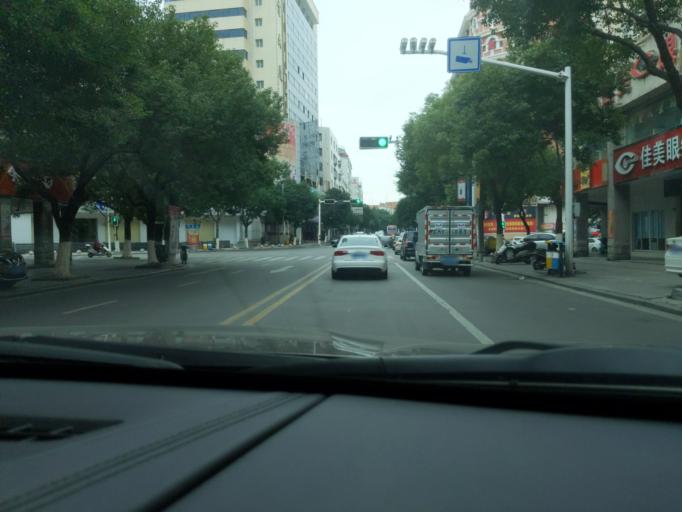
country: CN
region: Fujian
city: Shishi
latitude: 24.7357
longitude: 118.6332
